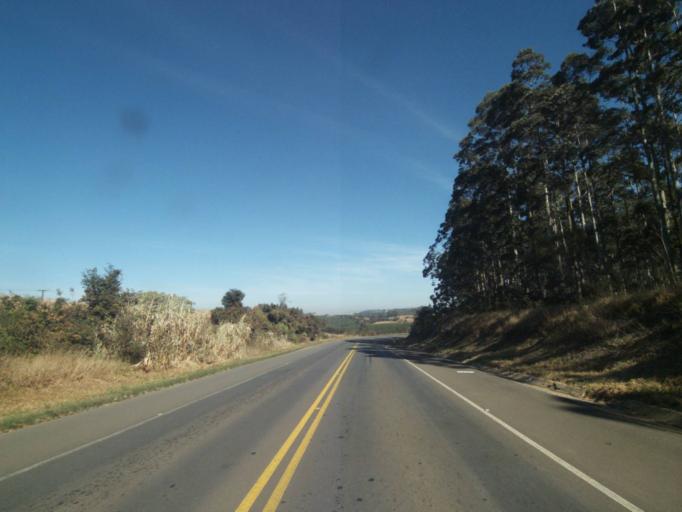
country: BR
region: Parana
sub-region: Tibagi
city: Tibagi
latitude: -24.8066
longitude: -50.4733
